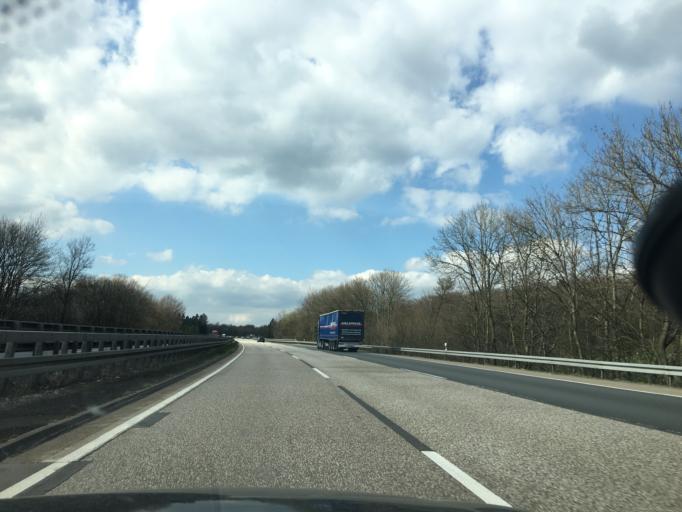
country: DE
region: North Rhine-Westphalia
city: Meinerzhagen
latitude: 51.1081
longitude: 7.6730
